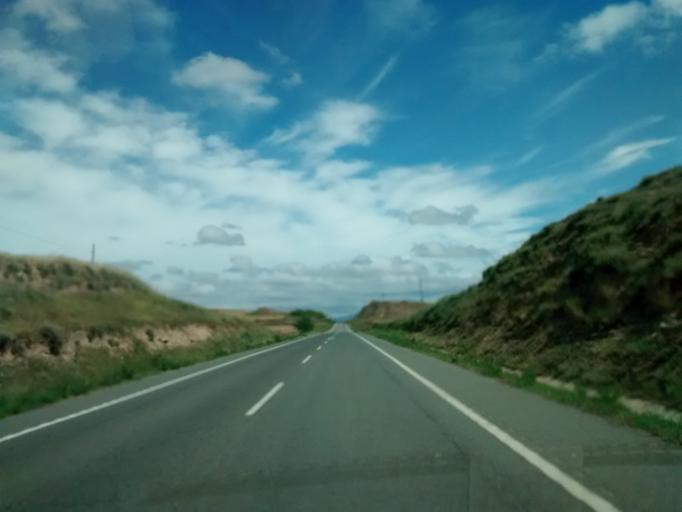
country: ES
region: La Rioja
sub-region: Provincia de La Rioja
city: Leza de Rio Leza
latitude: 42.3643
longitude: -2.3885
